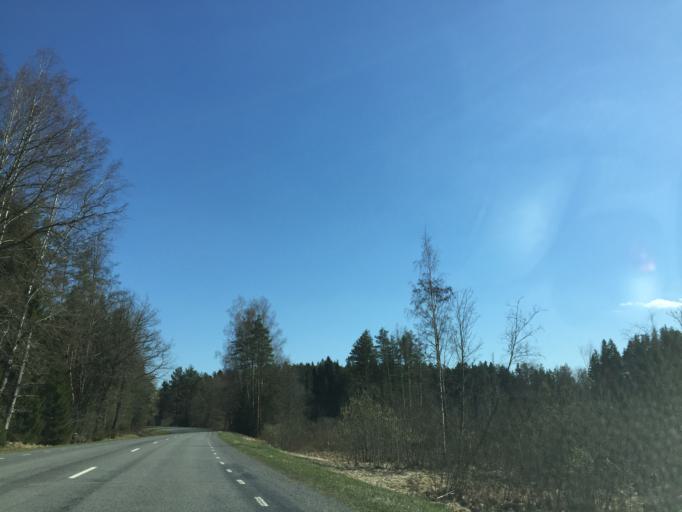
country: EE
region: Viljandimaa
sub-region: Viljandi linn
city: Viljandi
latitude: 58.2816
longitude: 25.5906
